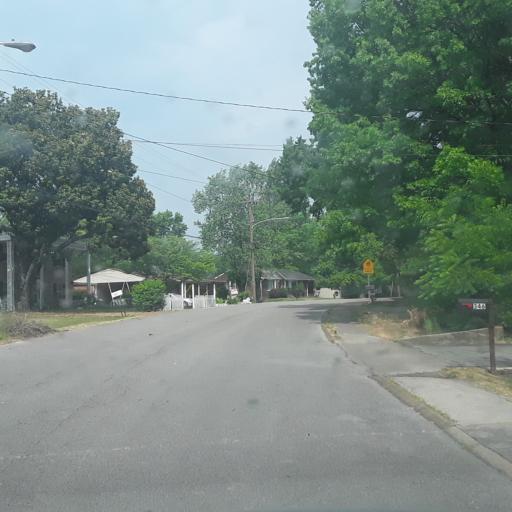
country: US
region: Tennessee
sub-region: Davidson County
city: Oak Hill
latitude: 36.0755
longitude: -86.7477
